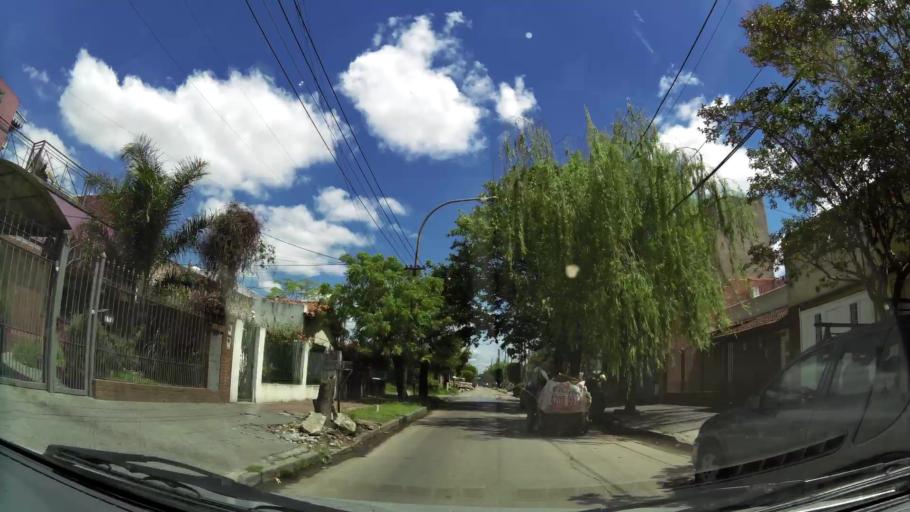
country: AR
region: Buenos Aires
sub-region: Partido de Lanus
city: Lanus
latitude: -34.7280
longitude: -58.4101
